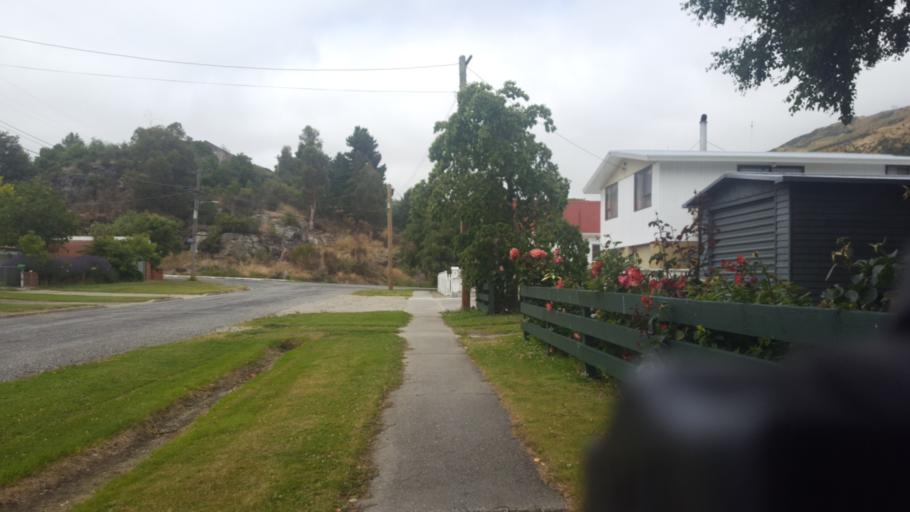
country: NZ
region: Otago
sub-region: Queenstown-Lakes District
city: Kingston
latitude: -45.5424
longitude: 169.3166
